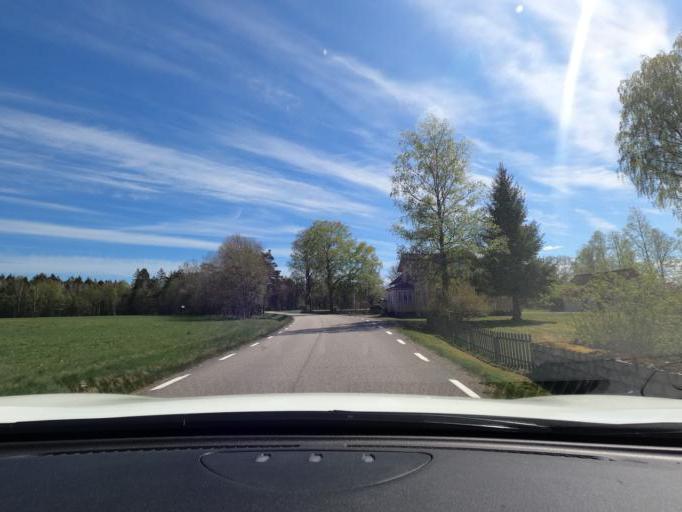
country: SE
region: Vaestra Goetaland
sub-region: Marks Kommun
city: Horred
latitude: 57.4237
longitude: 12.3593
